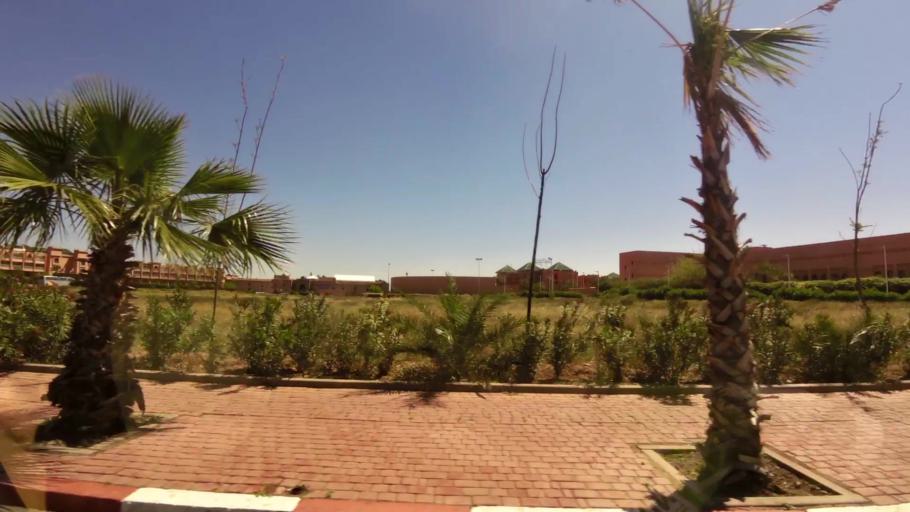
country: MA
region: Marrakech-Tensift-Al Haouz
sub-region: Marrakech
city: Marrakesh
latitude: 31.5949
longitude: -7.9928
